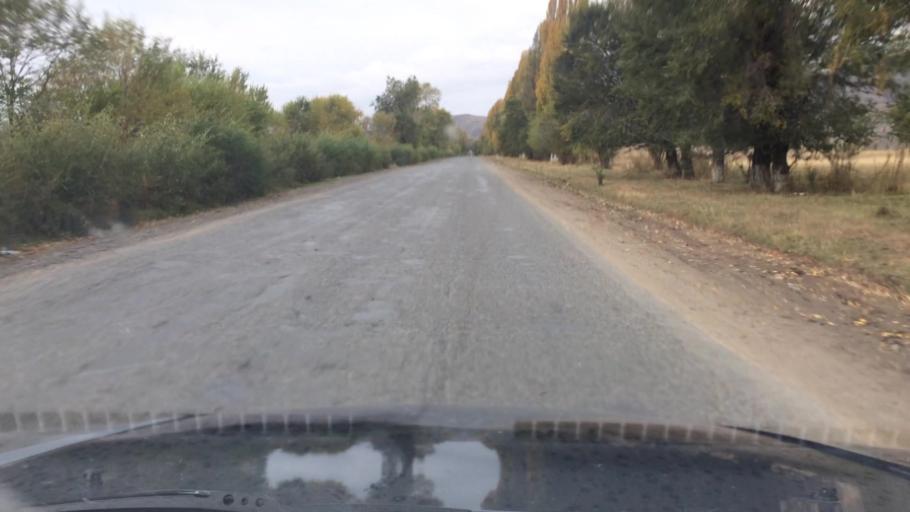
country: KG
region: Ysyk-Koel
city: Pokrovka
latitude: 42.7374
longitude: 77.9284
